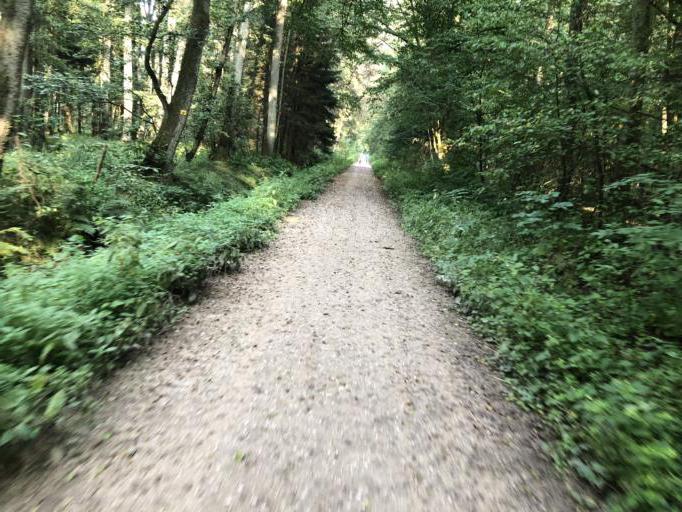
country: DE
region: Bavaria
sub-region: Regierungsbezirk Mittelfranken
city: Buckenhof
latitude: 49.5499
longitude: 11.0373
